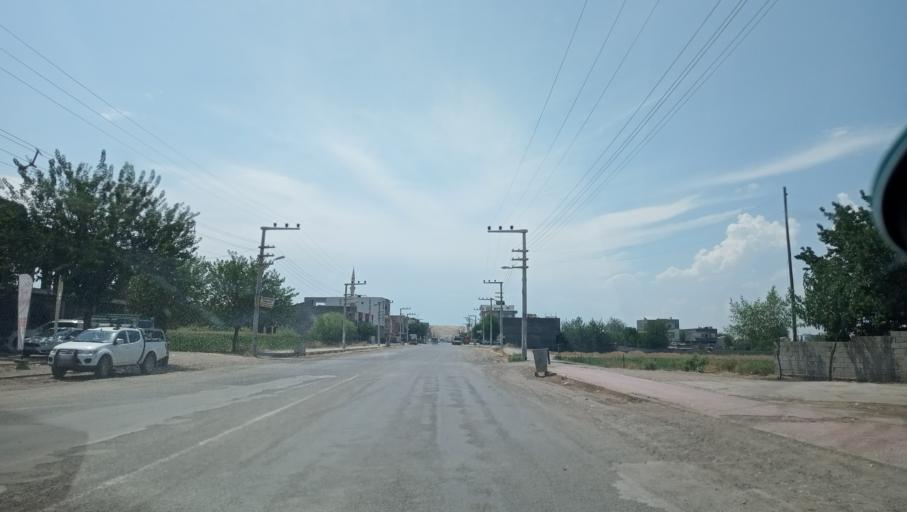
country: TR
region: Diyarbakir
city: Tepe
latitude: 37.7925
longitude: 40.7703
